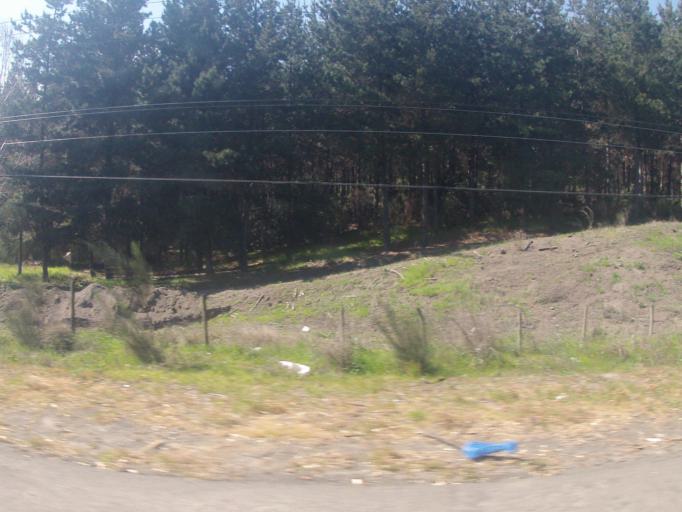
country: CL
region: Biobio
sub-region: Provincia de Biobio
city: Los Angeles
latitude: -37.3544
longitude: -72.3704
